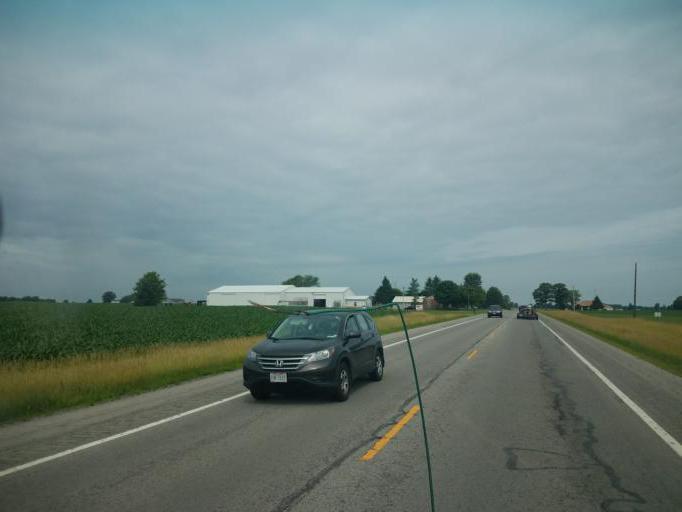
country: US
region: Ohio
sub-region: Hardin County
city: Kenton
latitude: 40.6792
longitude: -83.6747
